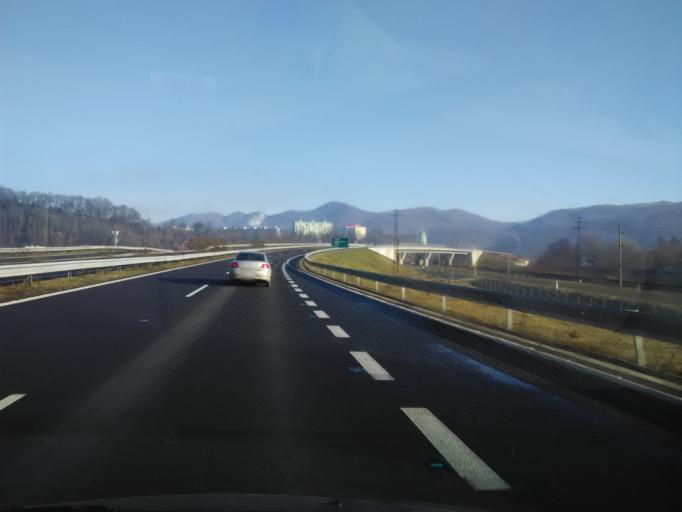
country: SK
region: Banskobystricky
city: Zarnovica
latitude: 48.4728
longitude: 18.7100
